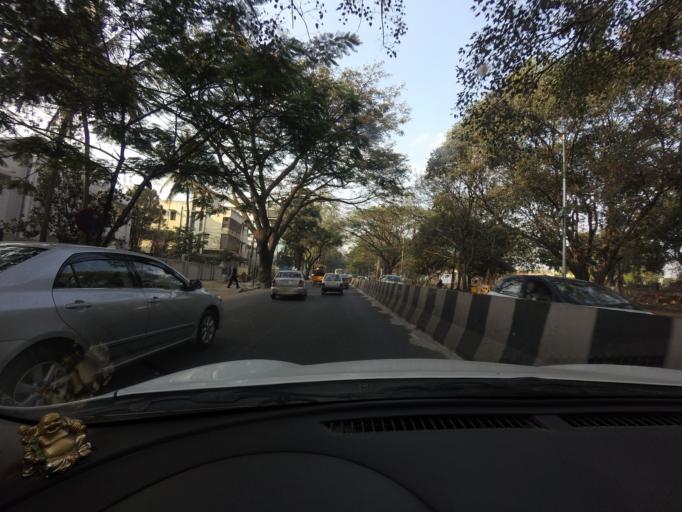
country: IN
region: Karnataka
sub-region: Bangalore Urban
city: Bangalore
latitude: 13.0050
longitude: 77.5840
